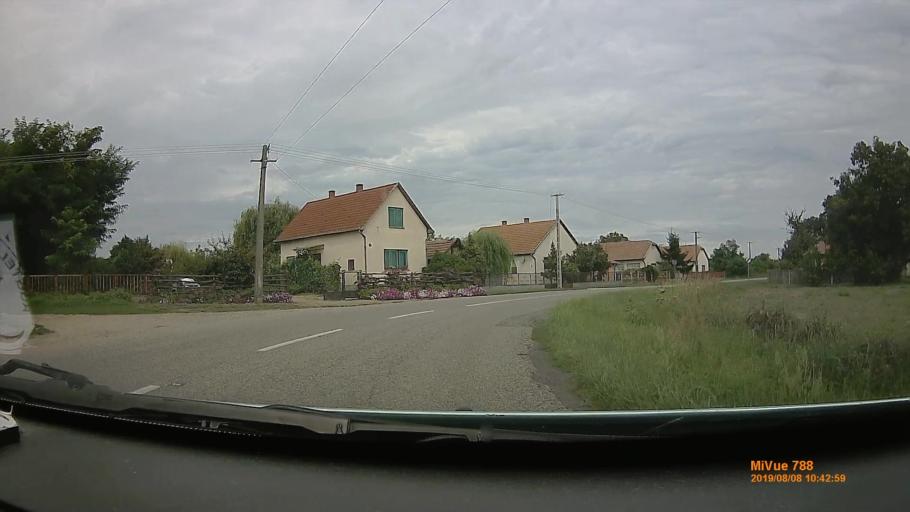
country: HU
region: Hajdu-Bihar
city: Nyiradony
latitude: 47.7183
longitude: 21.8774
